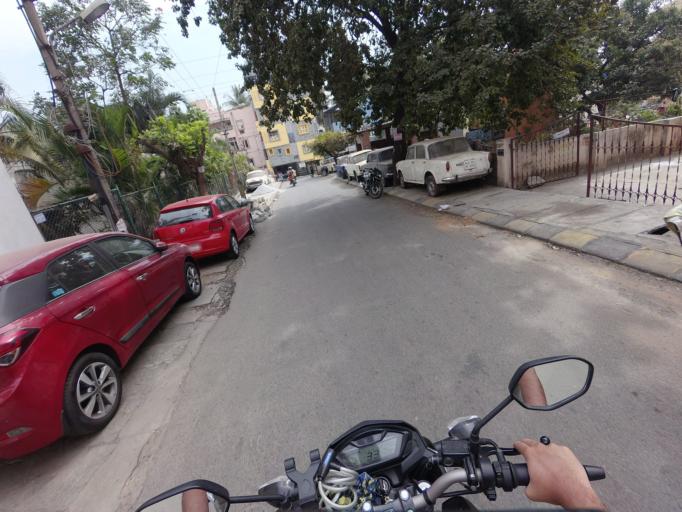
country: IN
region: Karnataka
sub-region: Bangalore Urban
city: Bangalore
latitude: 12.9721
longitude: 77.5335
